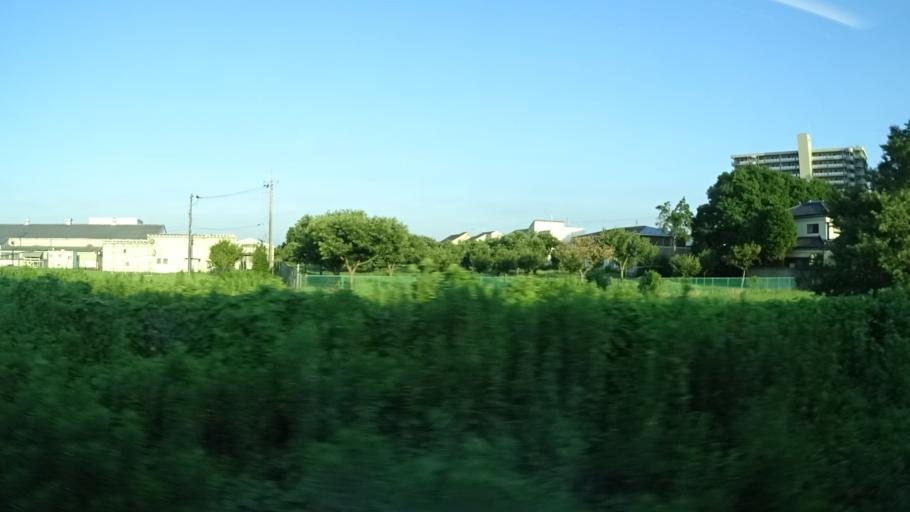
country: JP
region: Ibaraki
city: Ishioka
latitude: 36.1250
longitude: 140.2538
